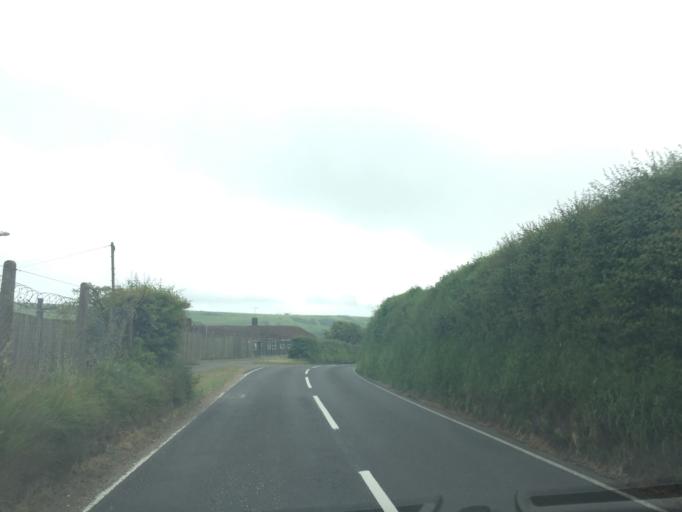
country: GB
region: England
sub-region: Dorset
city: Wool
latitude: 50.6321
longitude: -2.2350
